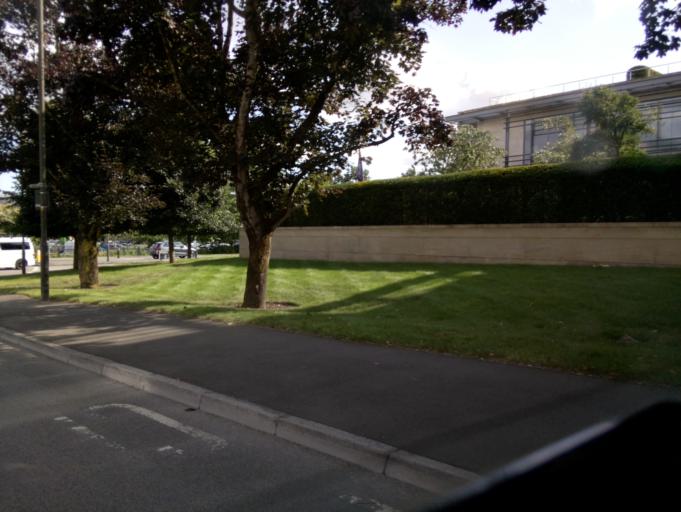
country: GB
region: England
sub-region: Gloucestershire
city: Cirencester
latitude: 51.7144
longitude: -1.9723
